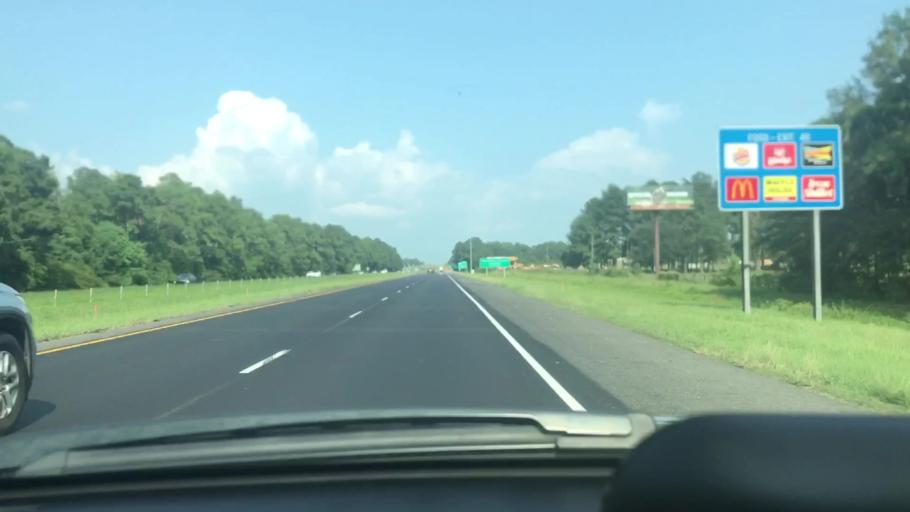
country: US
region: Louisiana
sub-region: Tangipahoa Parish
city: Hammond
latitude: 30.4788
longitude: -90.4737
